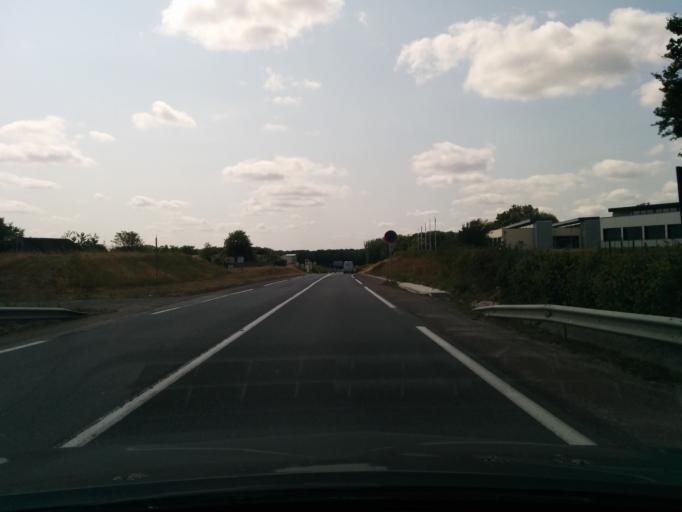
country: FR
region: Centre
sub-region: Departement du Cher
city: Vierzon
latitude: 47.2460
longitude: 2.0719
